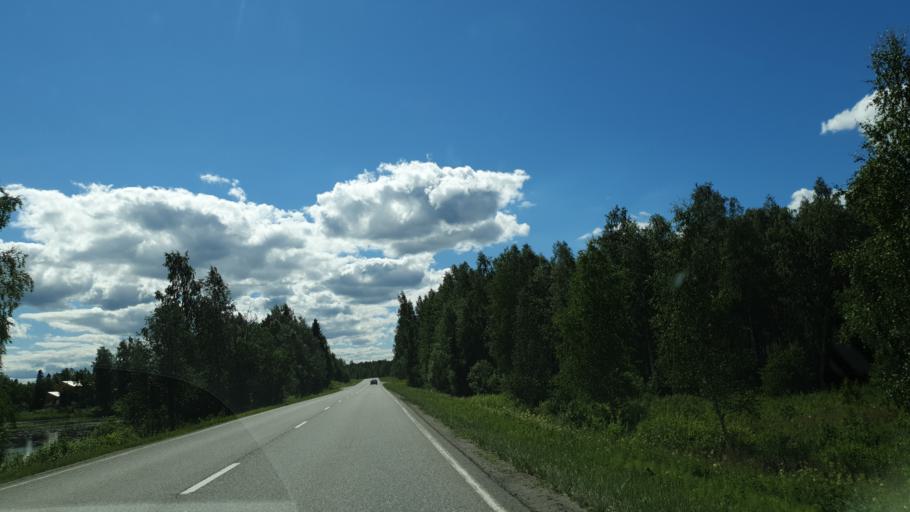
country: FI
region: Northern Savo
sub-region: Koillis-Savo
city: Juankoski
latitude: 63.2636
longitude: 28.3041
